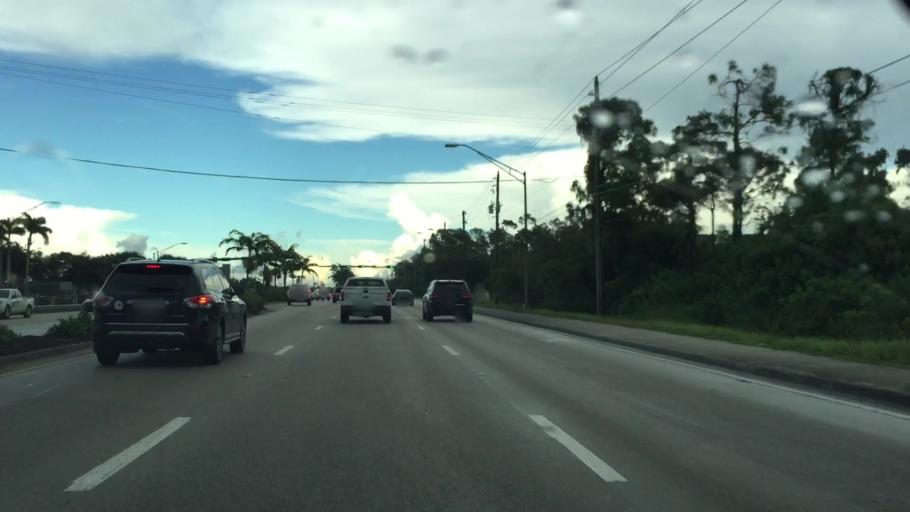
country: US
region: Florida
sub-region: Collier County
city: Vineyards
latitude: 26.2728
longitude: -81.7347
